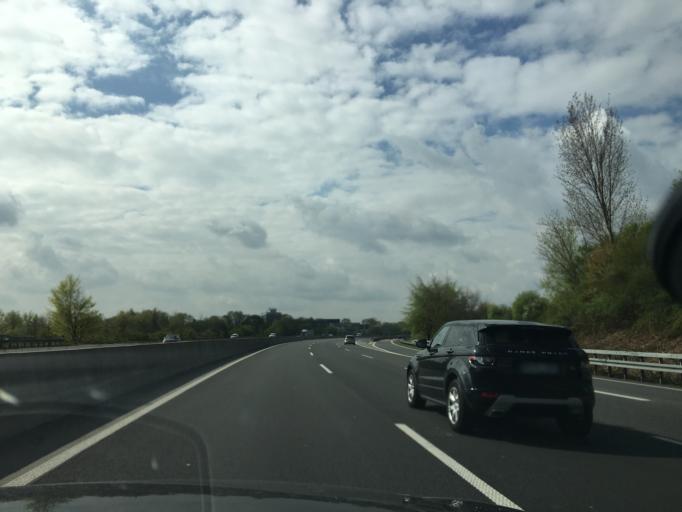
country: DE
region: North Rhine-Westphalia
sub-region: Regierungsbezirk Dusseldorf
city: Ratingen
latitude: 51.2811
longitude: 6.8039
